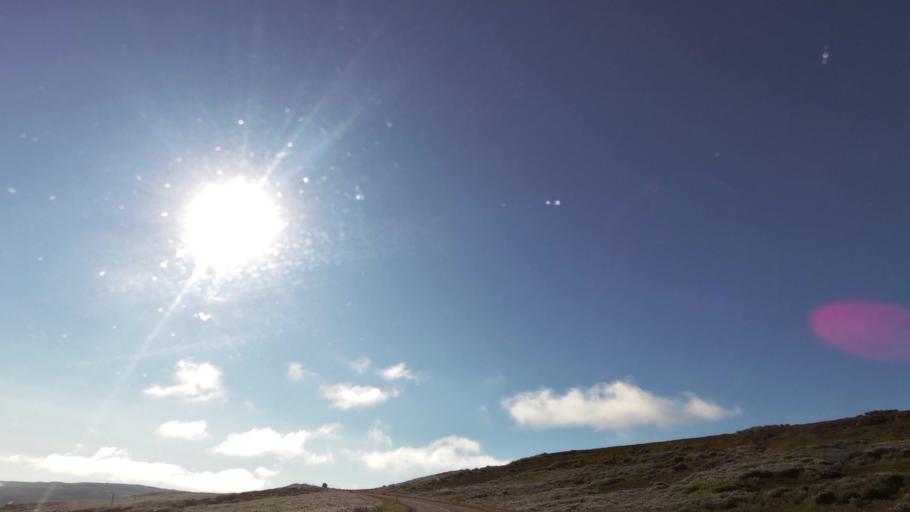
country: IS
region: West
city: Olafsvik
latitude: 65.5402
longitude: -23.8613
